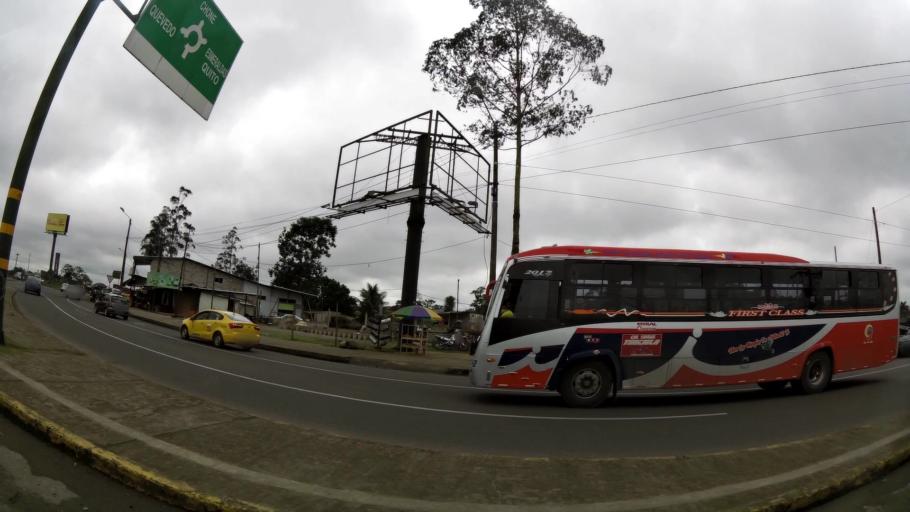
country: EC
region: Santo Domingo de los Tsachilas
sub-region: Canton Santo Domingo de los Colorados
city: Santo Domingo de los Colorados
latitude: -0.2500
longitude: -79.2017
